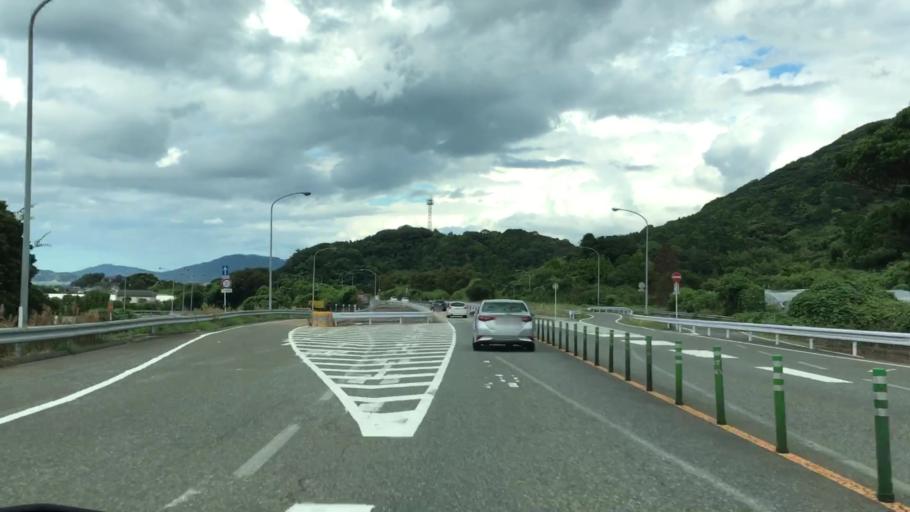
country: JP
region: Saga Prefecture
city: Karatsu
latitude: 33.4944
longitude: 130.0768
